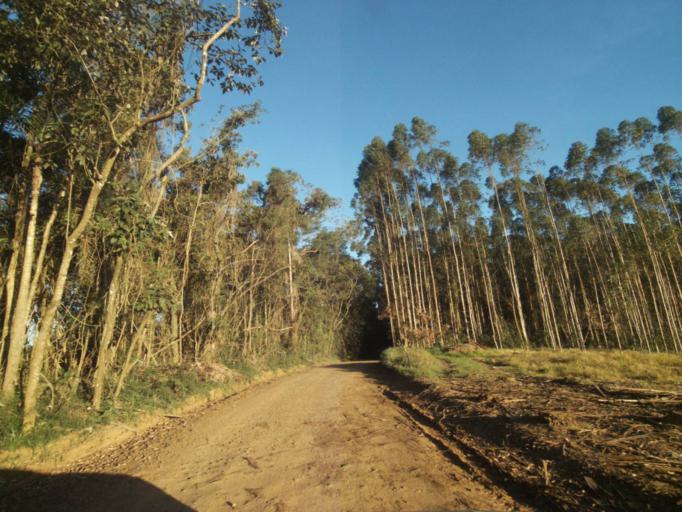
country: BR
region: Parana
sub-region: Telemaco Borba
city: Telemaco Borba
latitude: -24.4998
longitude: -50.5983
